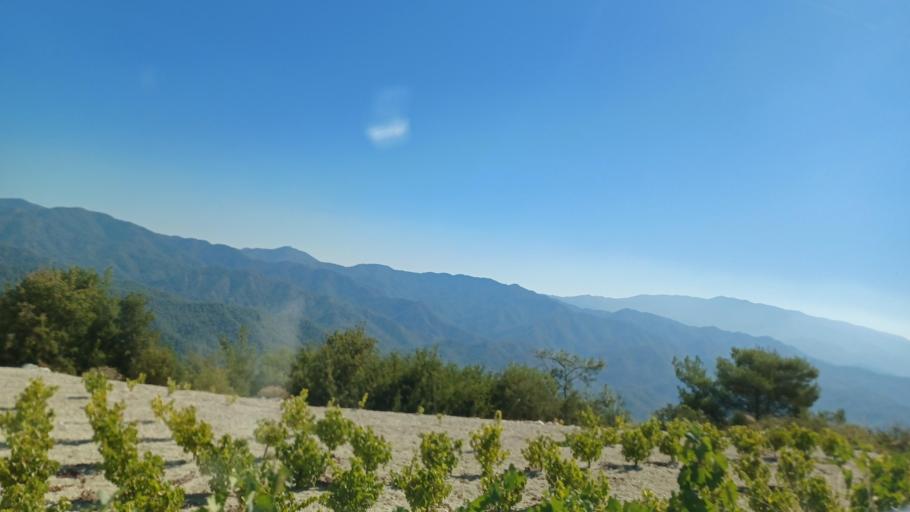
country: CY
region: Limassol
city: Pachna
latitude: 34.9077
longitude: 32.6415
